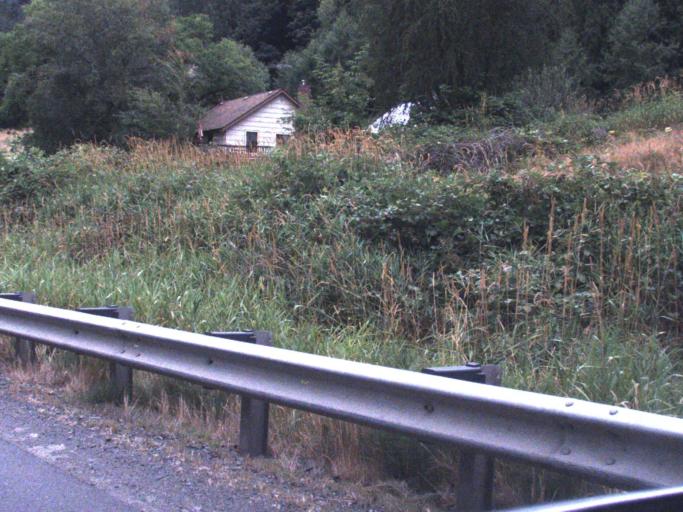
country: US
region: Washington
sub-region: King County
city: Duvall
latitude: 47.7706
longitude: -121.9558
